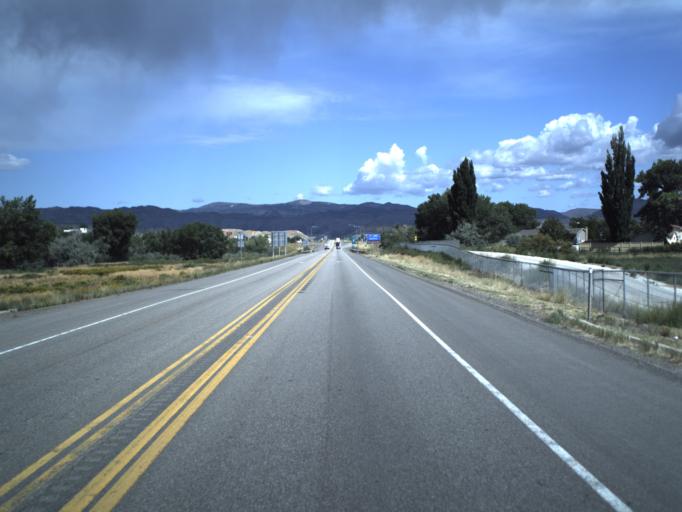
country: US
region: Utah
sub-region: Carbon County
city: Price
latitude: 39.5931
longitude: -110.8211
